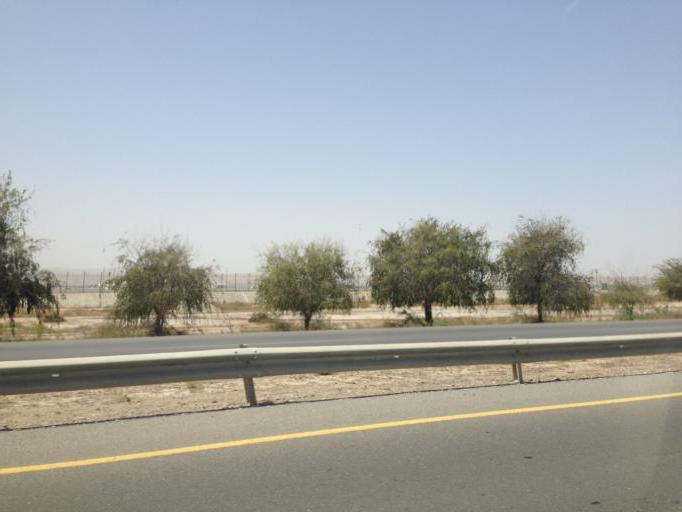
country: OM
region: Muhafazat Masqat
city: As Sib al Jadidah
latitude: 23.6159
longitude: 58.2878
